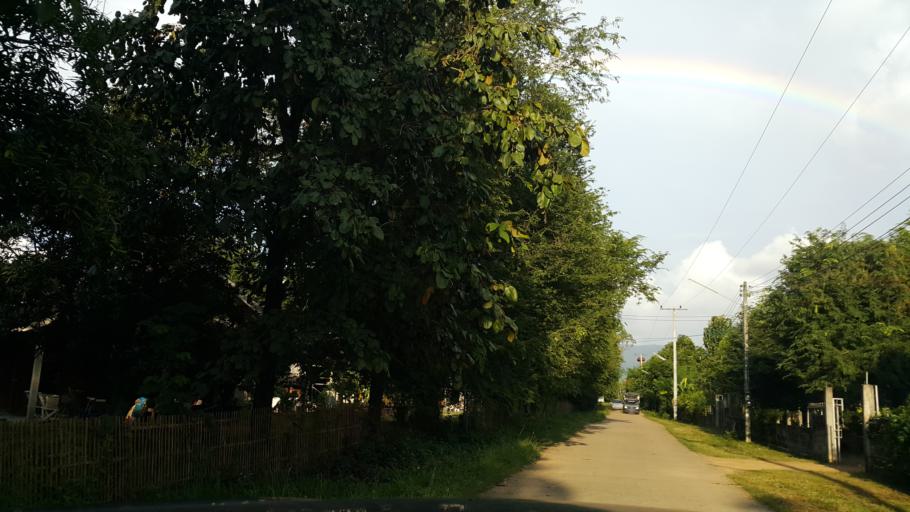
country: TH
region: Chiang Mai
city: Mae On
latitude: 18.7380
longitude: 99.2356
